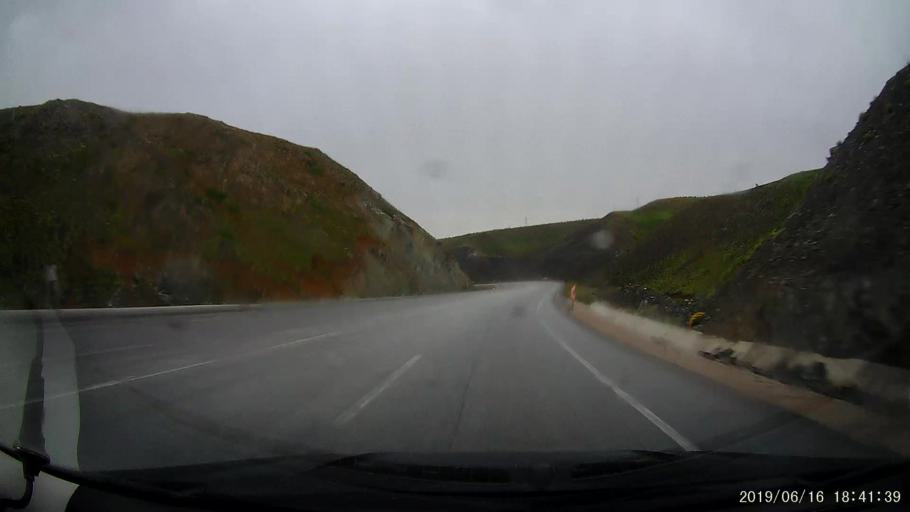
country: TR
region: Erzincan
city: Doganbeyli
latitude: 39.8722
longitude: 39.1248
